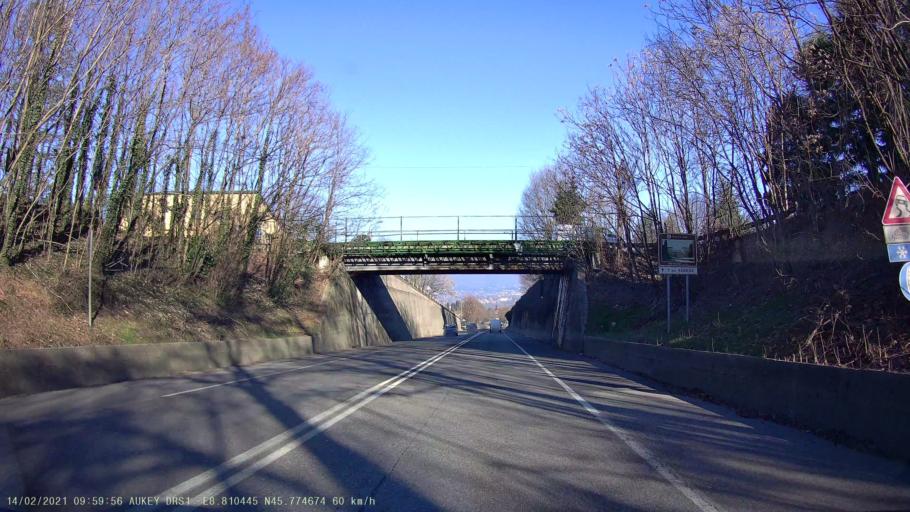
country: IT
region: Lombardy
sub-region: Provincia di Varese
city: Buguggiate
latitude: 45.7751
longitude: 8.8103
